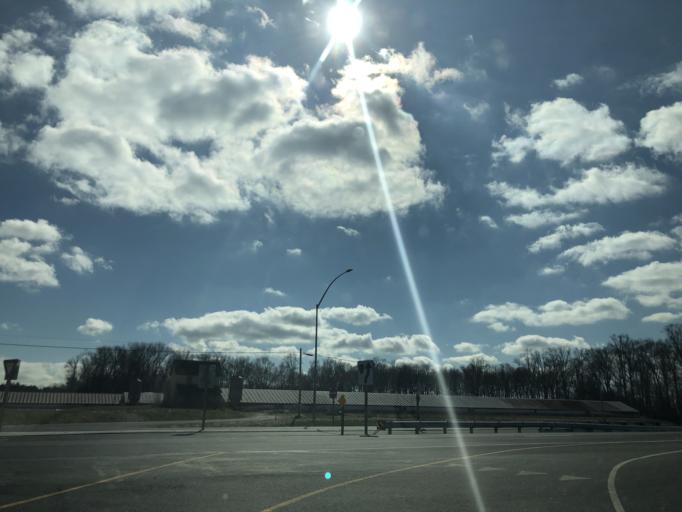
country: US
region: Maryland
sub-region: Worcester County
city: Snow Hill
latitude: 38.2288
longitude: -75.3392
